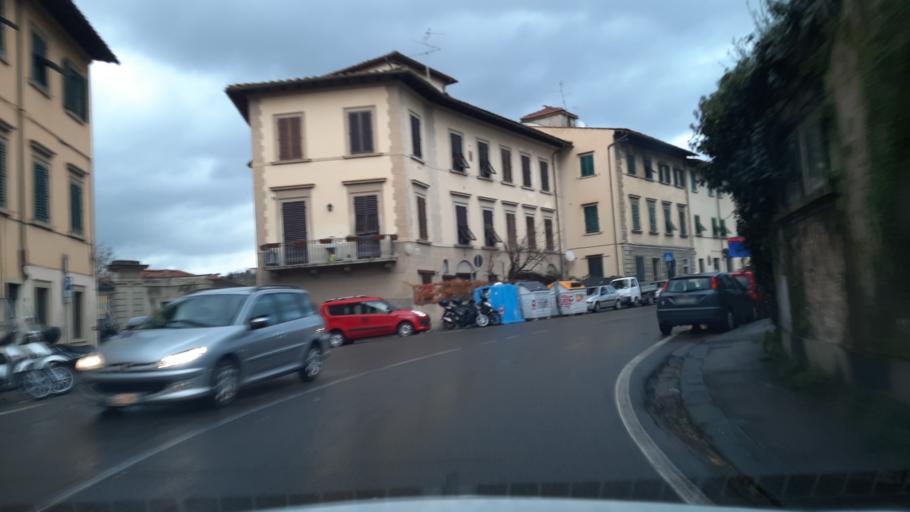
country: IT
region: Tuscany
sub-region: Province of Florence
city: Florence
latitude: 43.7981
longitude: 11.2623
